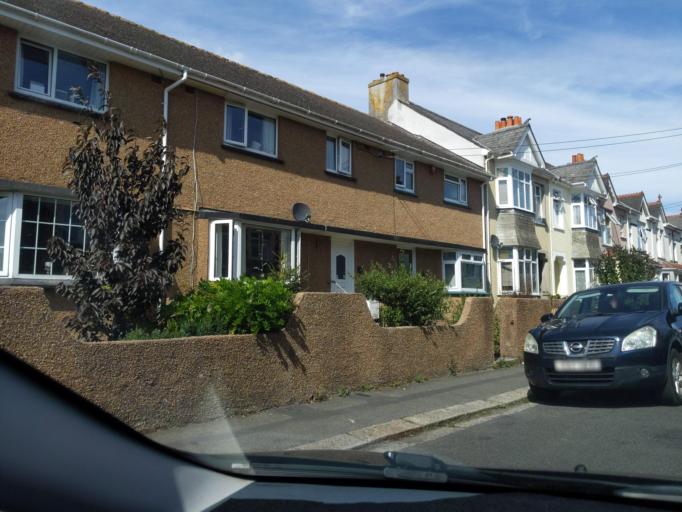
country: GB
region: England
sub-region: Cornwall
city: Torpoint
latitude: 50.3761
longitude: -4.2029
